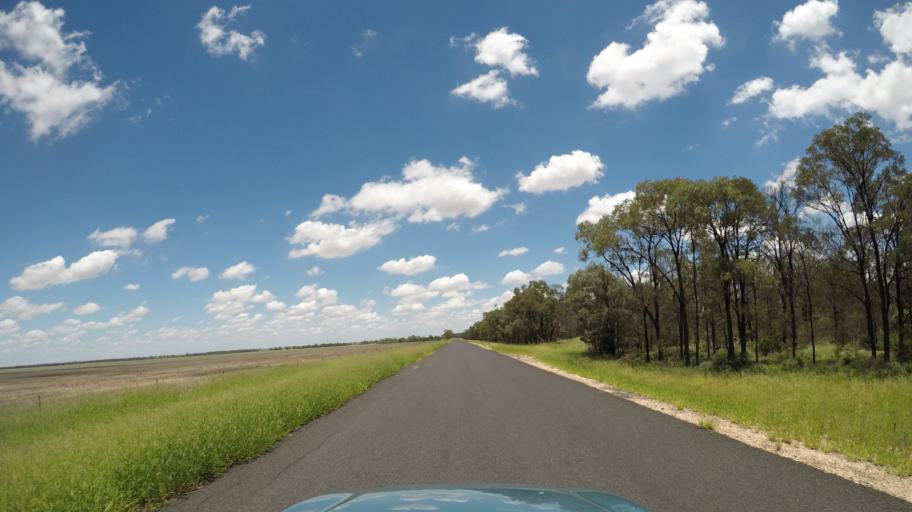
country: AU
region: Queensland
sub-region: Goondiwindi
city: Goondiwindi
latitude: -28.1580
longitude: 150.3884
